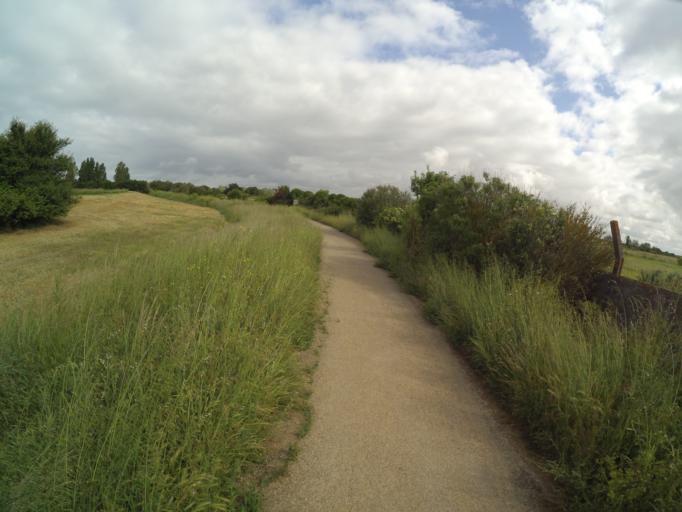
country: FR
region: Poitou-Charentes
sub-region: Departement de la Charente-Maritime
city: Angoulins
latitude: 46.1115
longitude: -1.1211
